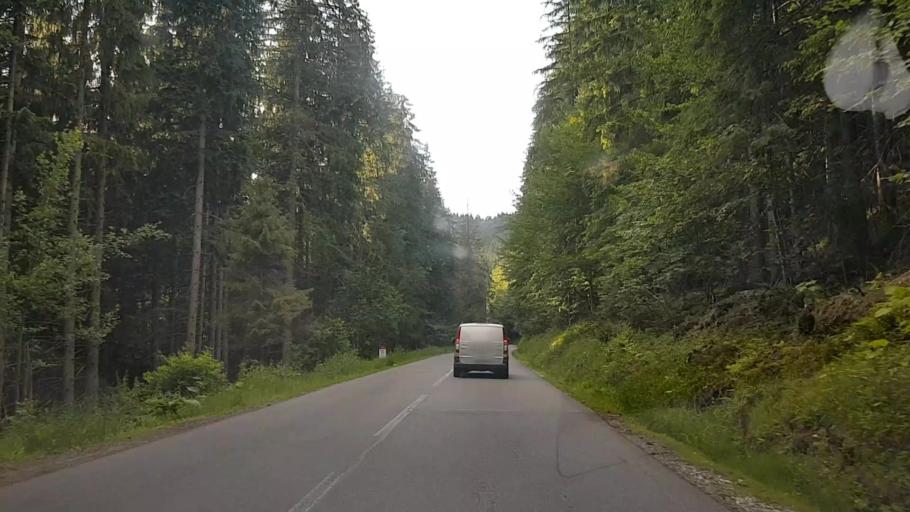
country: RO
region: Harghita
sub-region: Comuna Varsag
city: Varsag
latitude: 46.6698
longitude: 25.3301
